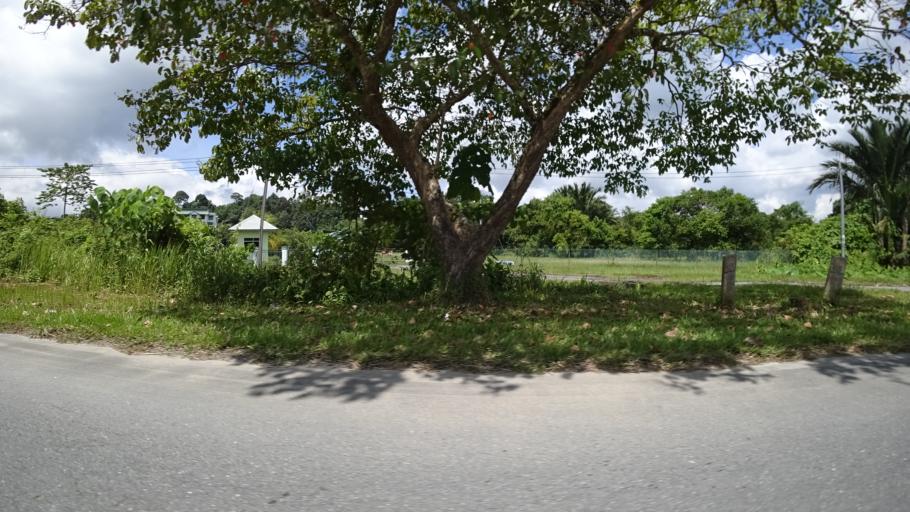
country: BN
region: Tutong
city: Tutong
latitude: 4.7298
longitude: 114.8044
